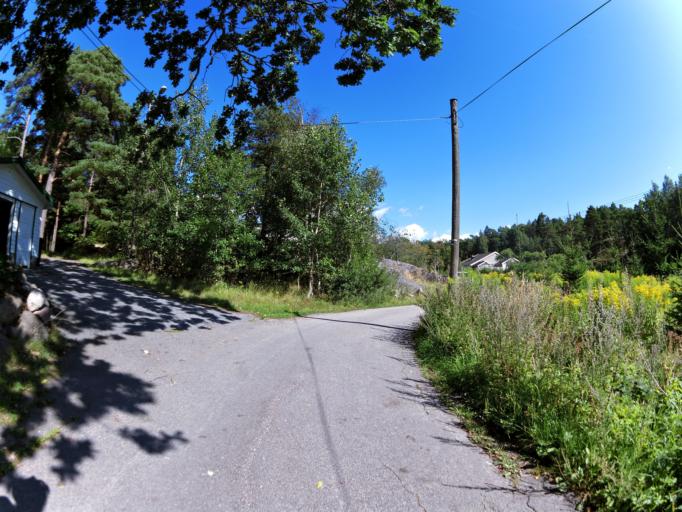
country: NO
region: Ostfold
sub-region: Fredrikstad
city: Fredrikstad
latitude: 59.1781
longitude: 10.8429
